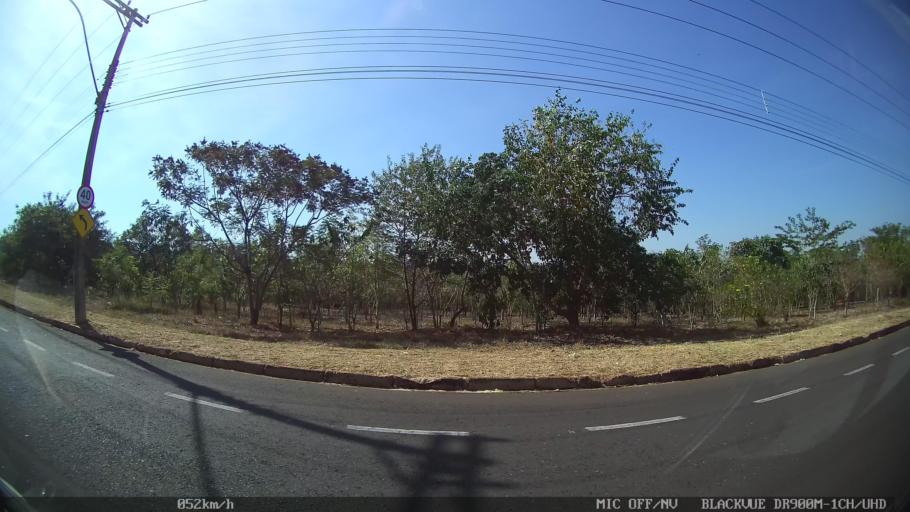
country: BR
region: Sao Paulo
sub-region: Sao Jose Do Rio Preto
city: Sao Jose do Rio Preto
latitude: -20.7917
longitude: -49.4346
